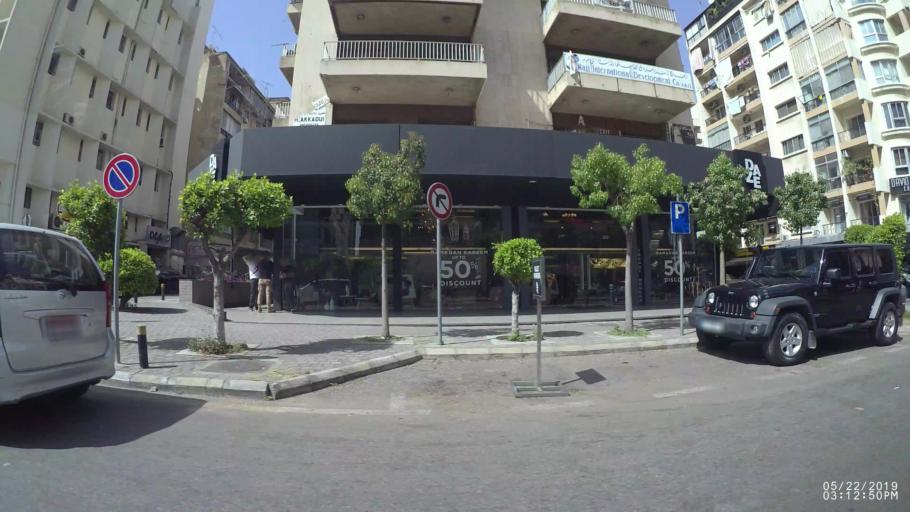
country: LB
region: Beyrouth
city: Beirut
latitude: 33.8804
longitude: 35.4924
